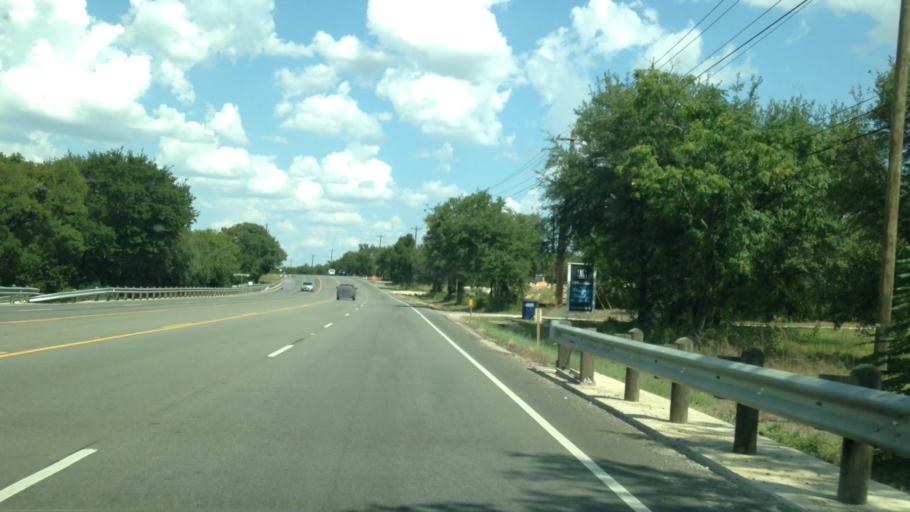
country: US
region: Texas
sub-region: Williamson County
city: Georgetown
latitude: 30.6311
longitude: -97.7469
